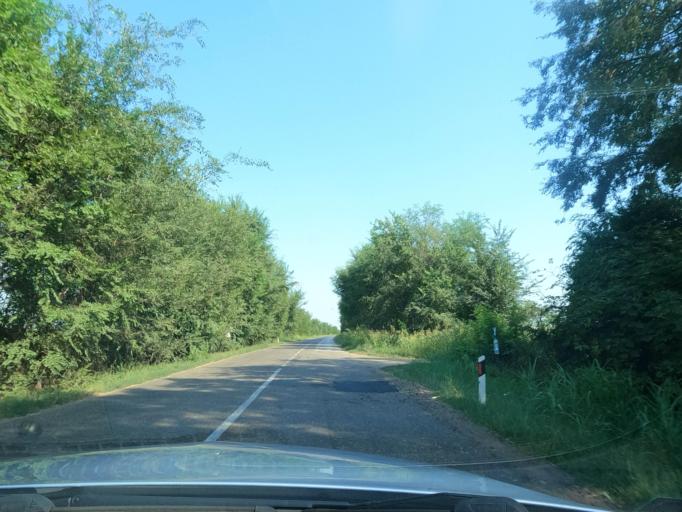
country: RS
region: Autonomna Pokrajina Vojvodina
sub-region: Juznobacki Okrug
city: Becej
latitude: 45.6618
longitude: 19.9502
